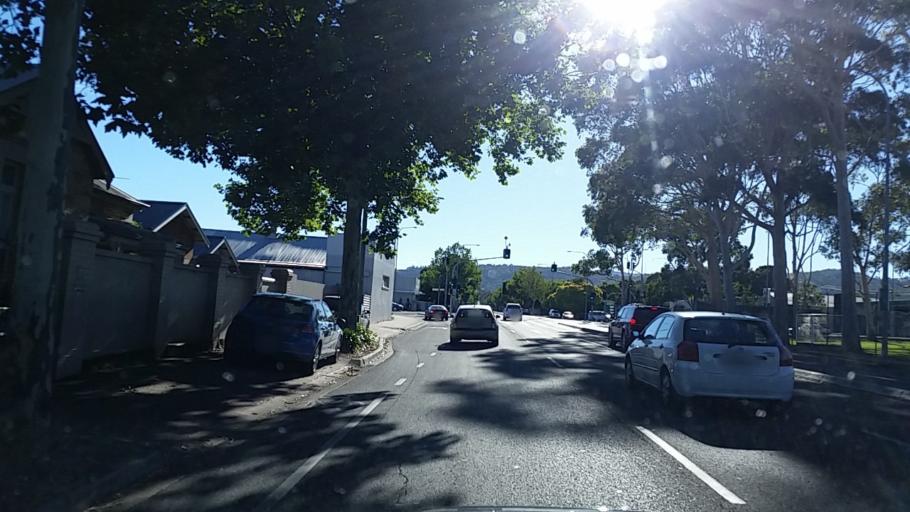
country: AU
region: South Australia
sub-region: Unley
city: Unley Park
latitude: -34.9654
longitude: 138.6075
